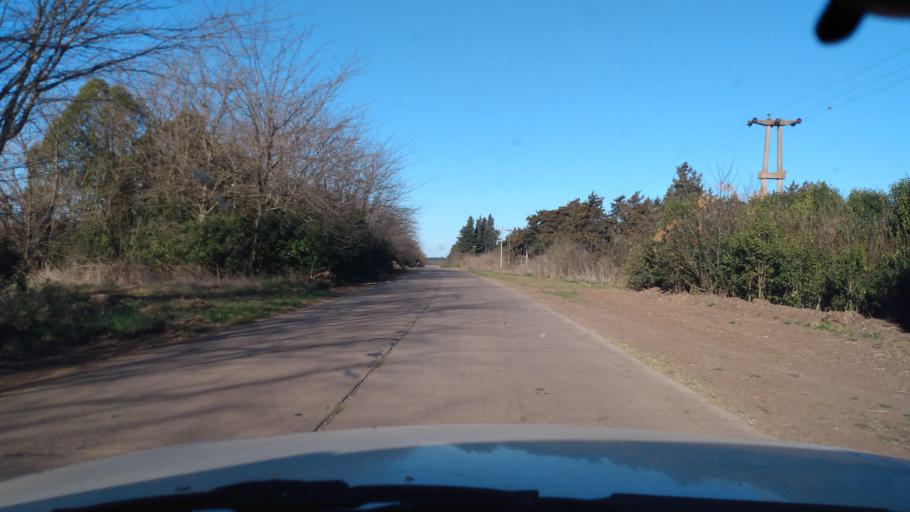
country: AR
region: Buenos Aires
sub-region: Partido de Mercedes
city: Mercedes
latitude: -34.6131
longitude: -59.2797
